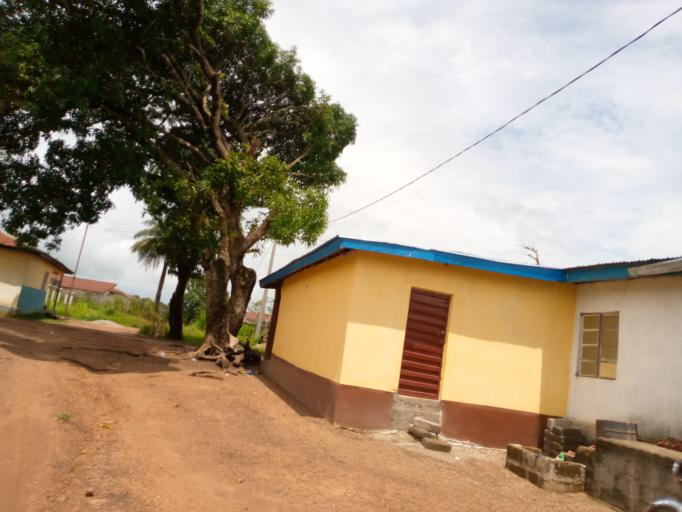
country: SL
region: Northern Province
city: Magburaka
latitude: 8.7266
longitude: -11.9360
